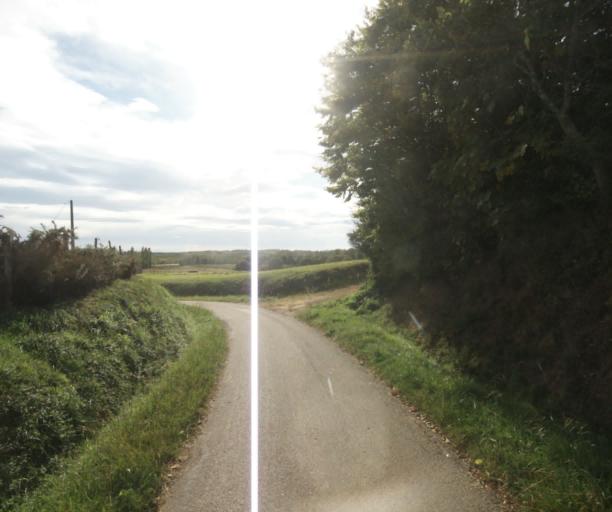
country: FR
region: Midi-Pyrenees
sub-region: Departement du Gers
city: Cazaubon
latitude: 43.8704
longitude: -0.1197
